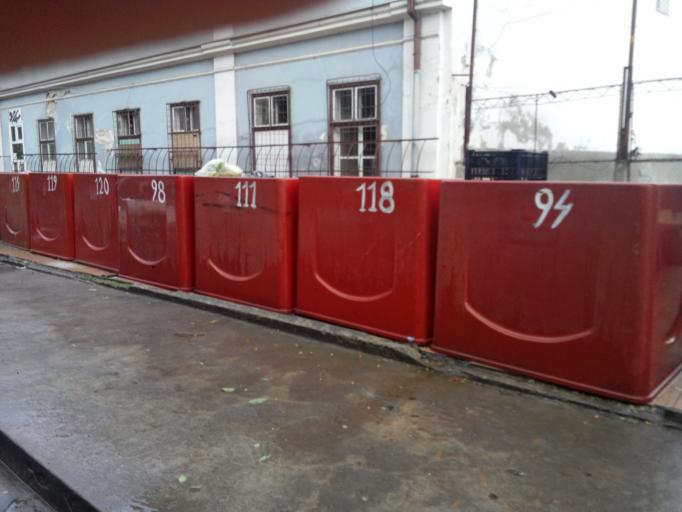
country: RO
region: Cluj
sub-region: Municipiul Cluj-Napoca
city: Cluj-Napoca
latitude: 46.7739
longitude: 23.5952
